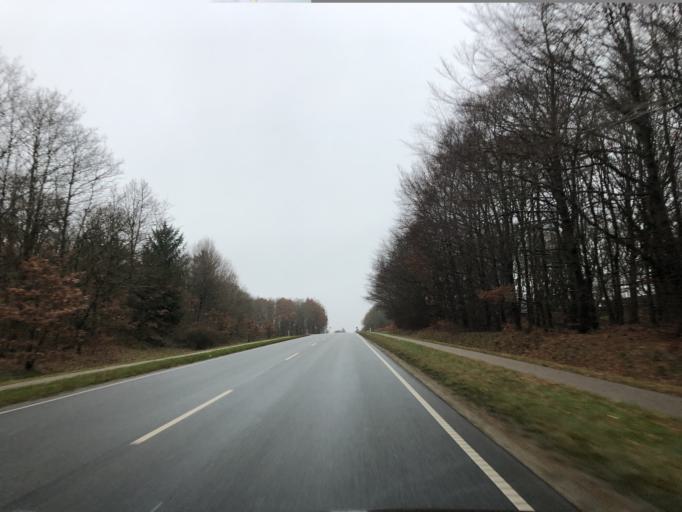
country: DK
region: Central Jutland
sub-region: Herning Kommune
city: Lind
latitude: 56.0928
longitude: 8.9806
